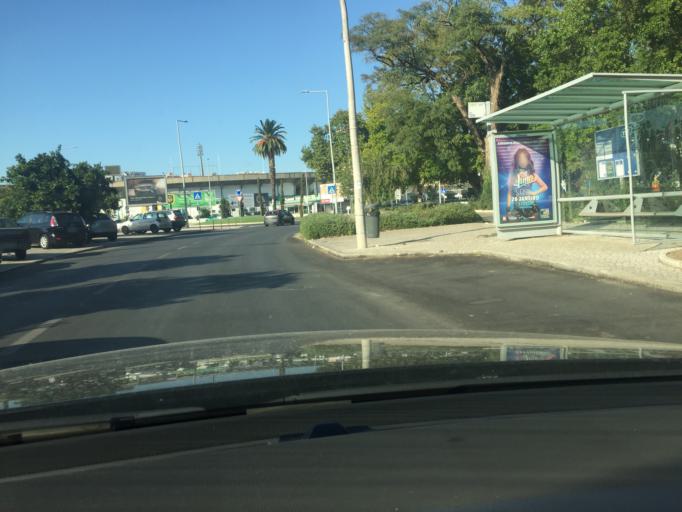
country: PT
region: Setubal
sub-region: Setubal
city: Setubal
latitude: 38.5291
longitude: -8.8921
